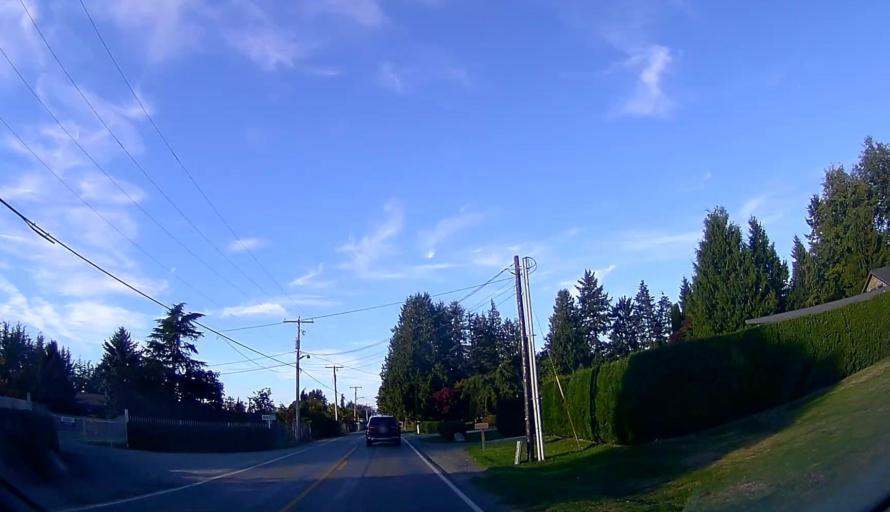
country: US
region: Washington
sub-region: Skagit County
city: Burlington
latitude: 48.4554
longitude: -122.3571
